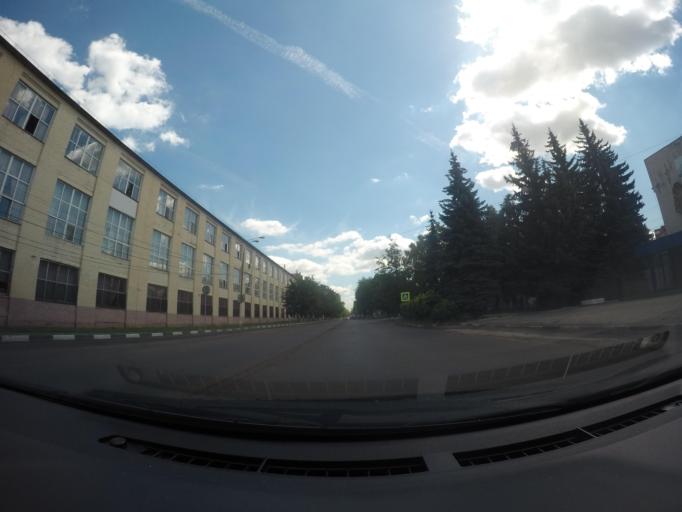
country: RU
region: Moskovskaya
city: Lyubertsy
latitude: 55.6844
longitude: 37.8747
